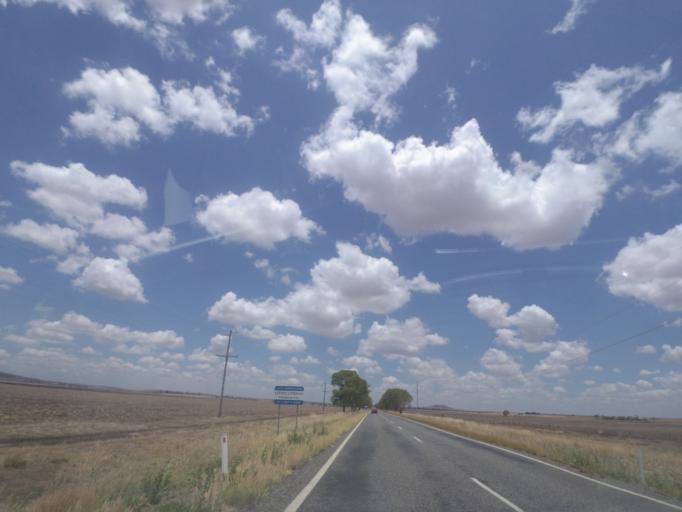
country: AU
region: Queensland
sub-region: Toowoomba
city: Top Camp
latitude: -27.9151
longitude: 151.9809
